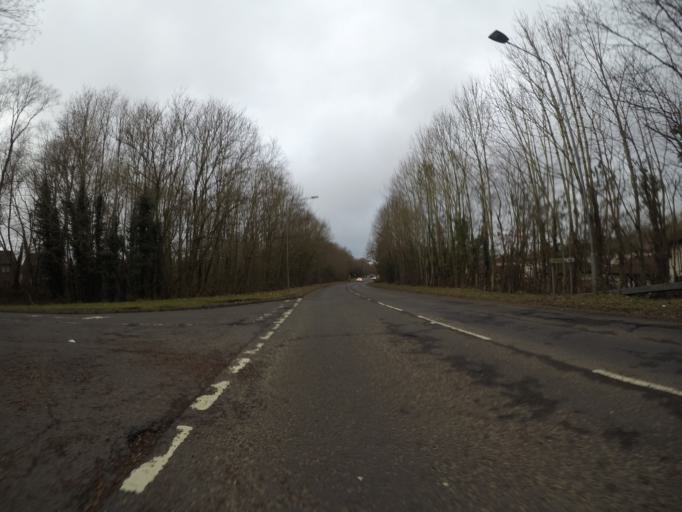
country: GB
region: Scotland
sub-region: North Ayrshire
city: Irvine
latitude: 55.6308
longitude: -4.6329
